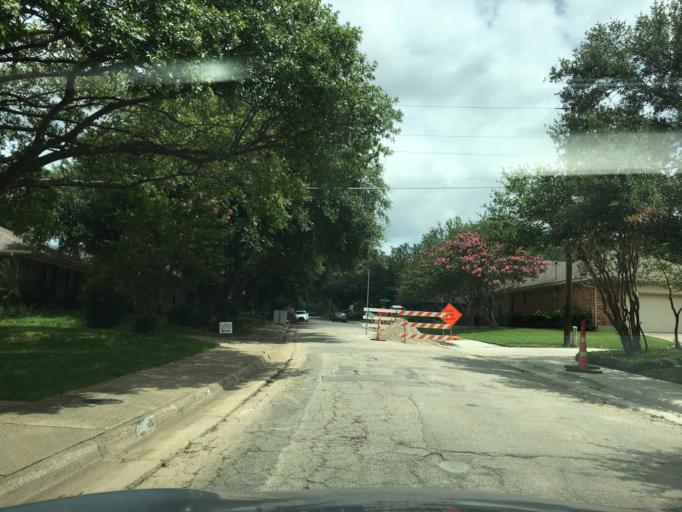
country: US
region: Texas
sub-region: Dallas County
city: Richardson
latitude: 32.9029
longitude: -96.7416
